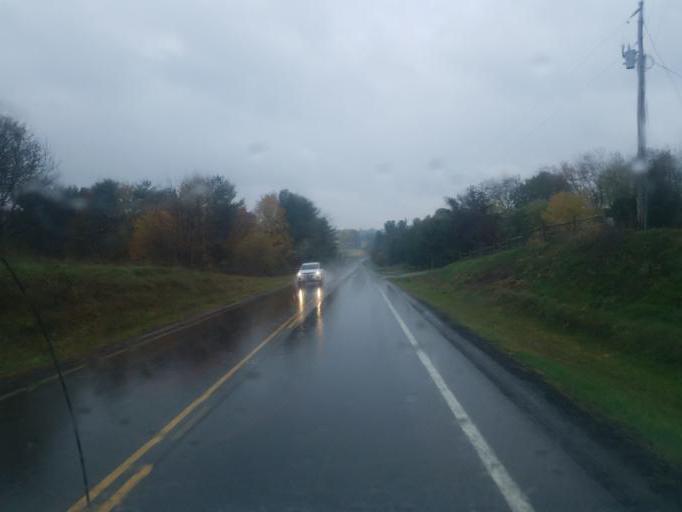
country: US
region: Ohio
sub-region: Licking County
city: Utica
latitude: 40.2535
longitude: -82.3299
